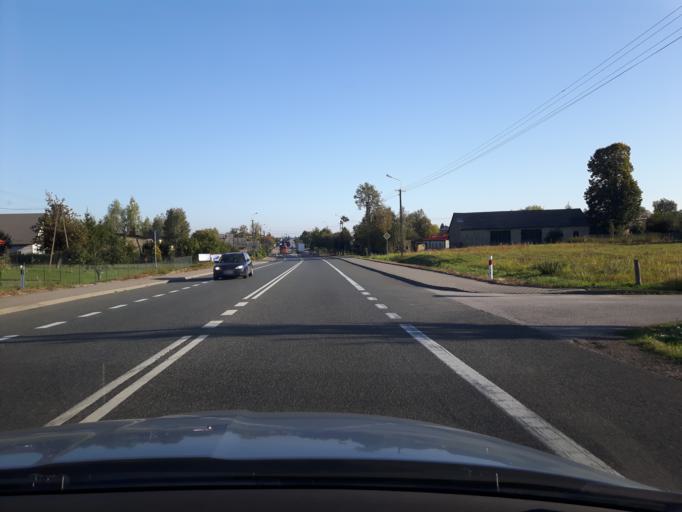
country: PL
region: Masovian Voivodeship
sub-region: Powiat mlawski
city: Mlawa
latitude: 53.1621
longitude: 20.4125
